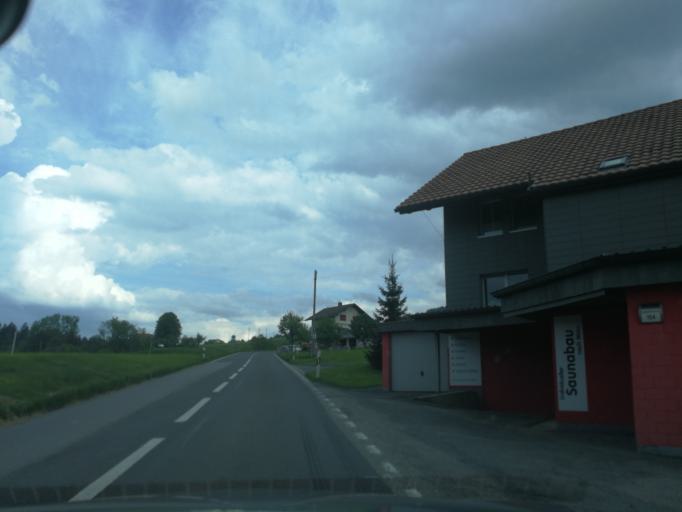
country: CH
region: Bern
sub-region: Bern-Mittelland District
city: Linden
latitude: 46.8385
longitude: 7.6481
